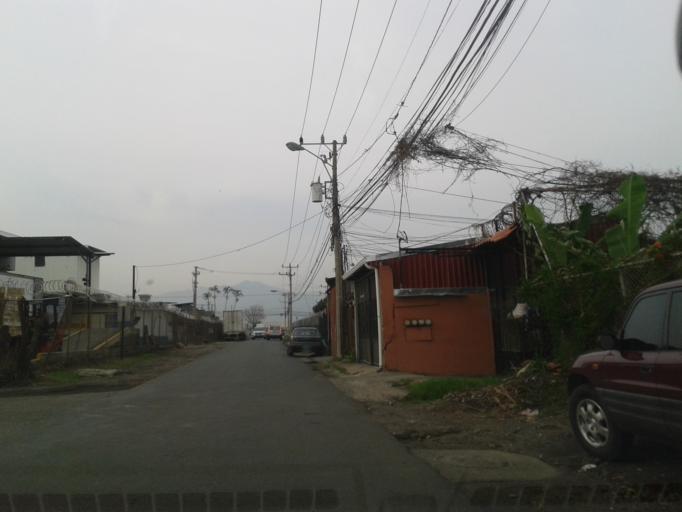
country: CR
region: Heredia
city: Llorente
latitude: 10.0038
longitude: -84.1608
